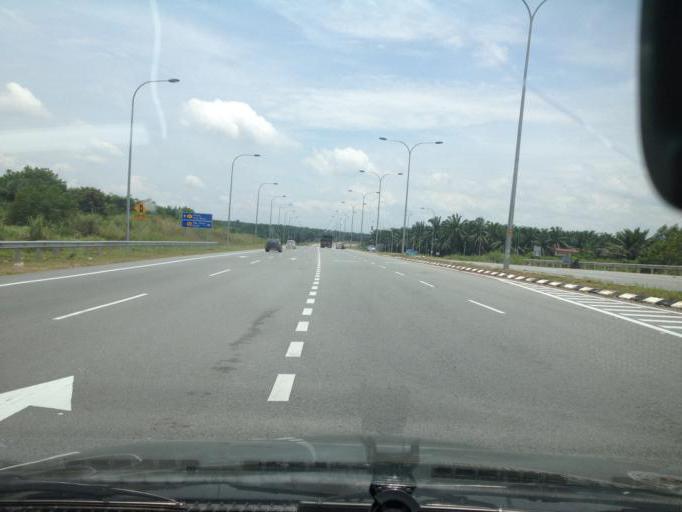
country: MY
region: Kedah
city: Sungai Petani
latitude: 5.6115
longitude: 100.5666
